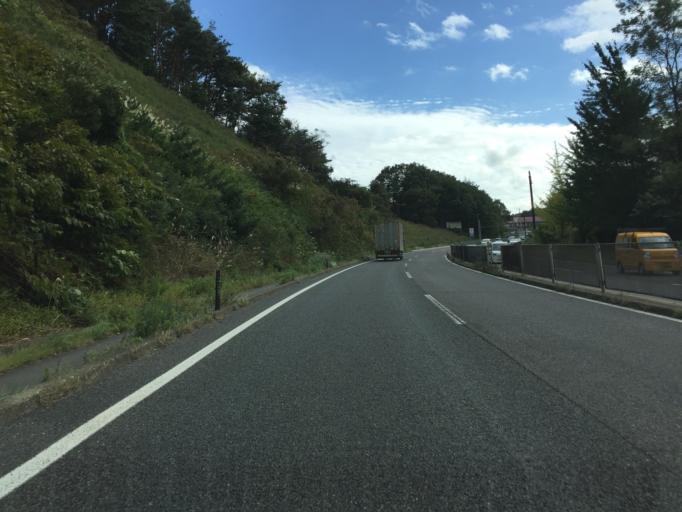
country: JP
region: Fukushima
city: Fukushima-shi
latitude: 37.7146
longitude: 140.4673
